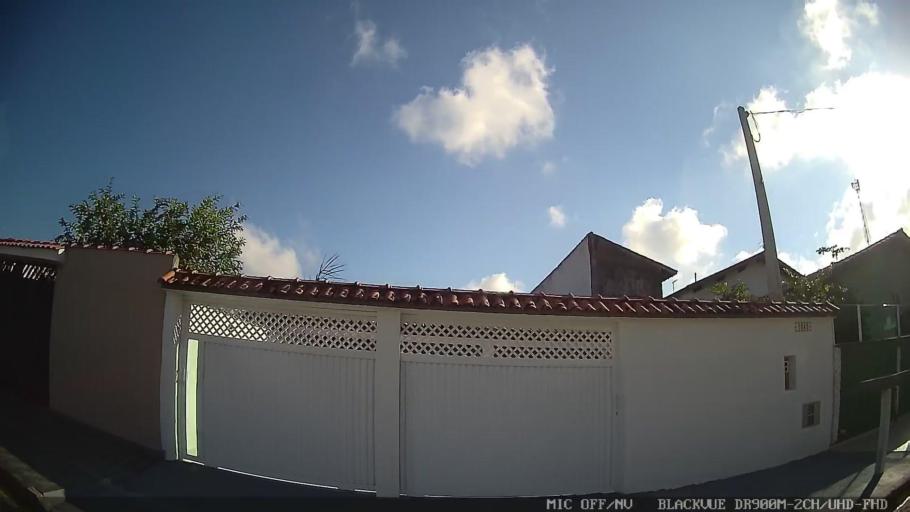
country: BR
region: Sao Paulo
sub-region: Peruibe
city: Peruibe
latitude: -24.2862
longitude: -46.9658
